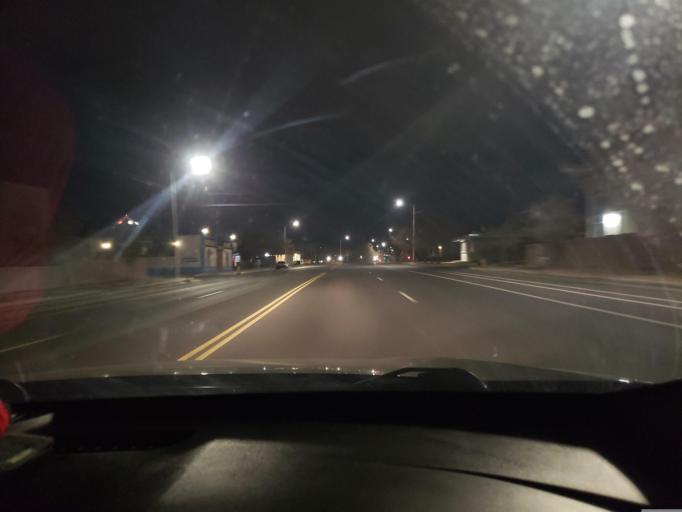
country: US
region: New Mexico
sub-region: Bernalillo County
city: Albuquerque
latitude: 35.0765
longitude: -106.6458
